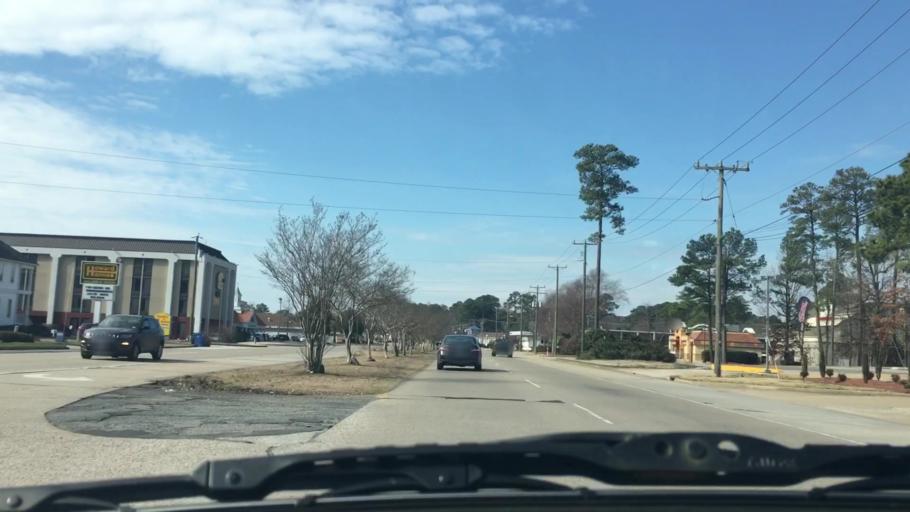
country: US
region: Virginia
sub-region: City of Portsmouth
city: Portsmouth Heights
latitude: 36.8640
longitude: -76.4059
